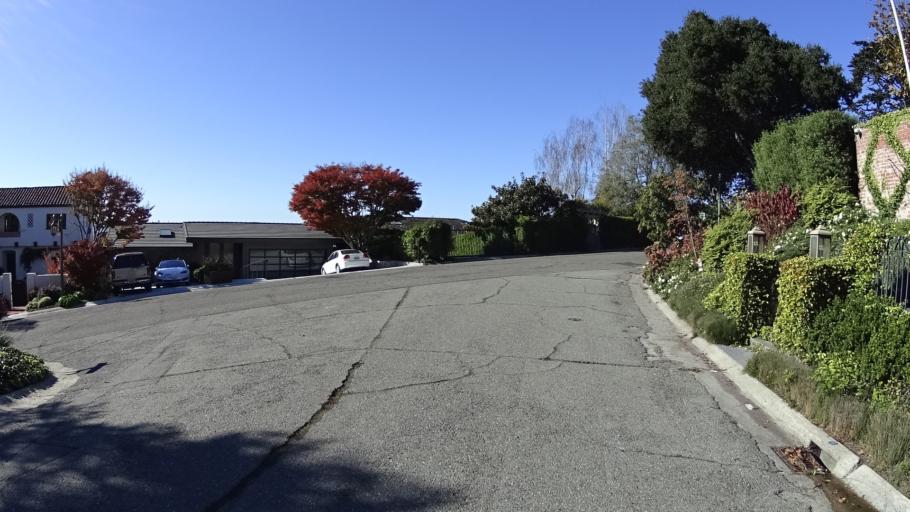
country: US
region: California
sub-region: Alameda County
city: Piedmont
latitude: 37.8418
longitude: -122.2419
